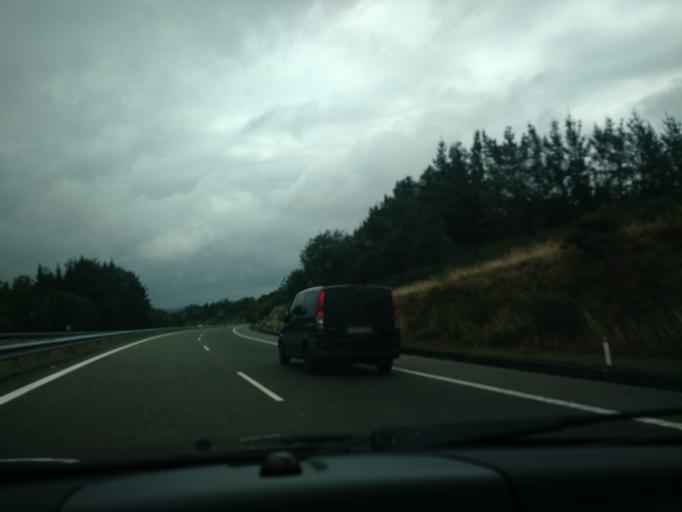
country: ES
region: Galicia
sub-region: Provincia da Coruna
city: Oroso
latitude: 42.9481
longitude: -8.4601
